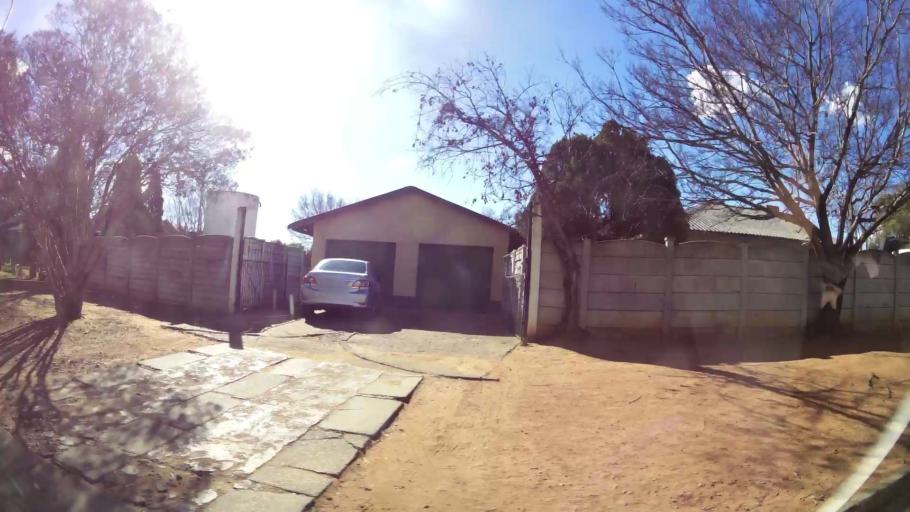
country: ZA
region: North-West
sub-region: Dr Kenneth Kaunda District Municipality
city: Klerksdorp
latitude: -26.8246
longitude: 26.6663
